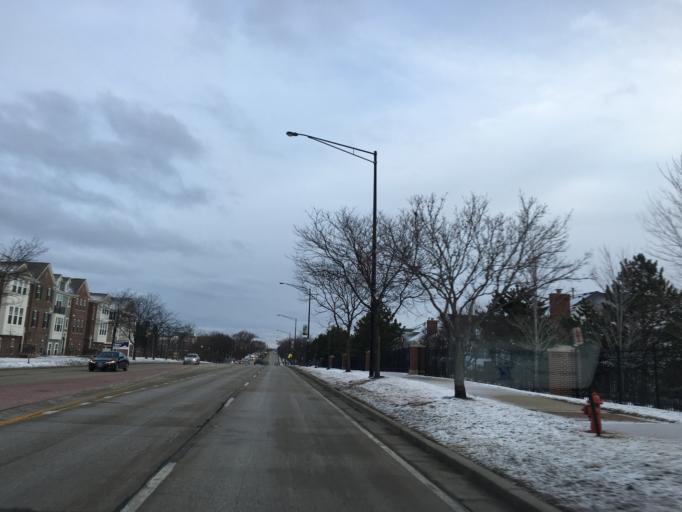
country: US
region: Illinois
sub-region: Cook County
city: Schaumburg
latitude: 42.0286
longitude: -88.0798
